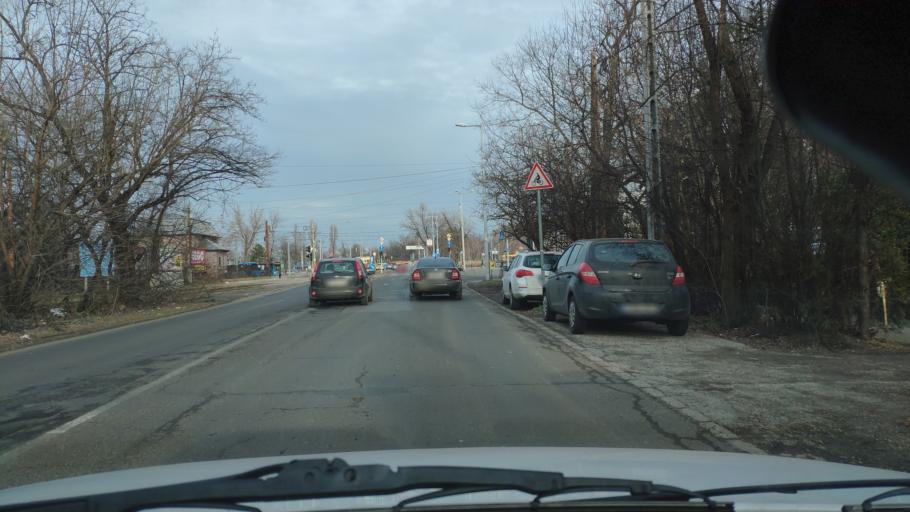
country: HU
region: Budapest
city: Budapest XIX. keruelet
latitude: 47.4631
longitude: 19.1260
